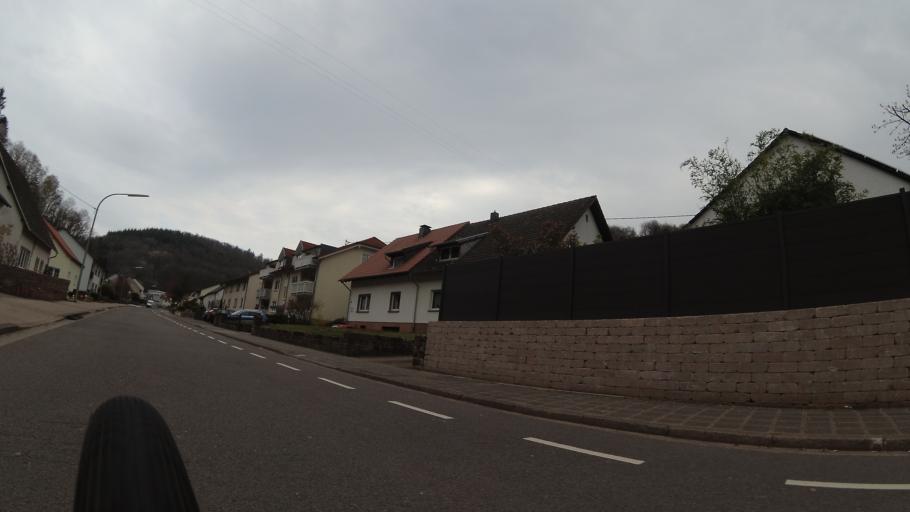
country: DE
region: Saarland
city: Merzig
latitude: 49.4604
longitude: 6.6430
